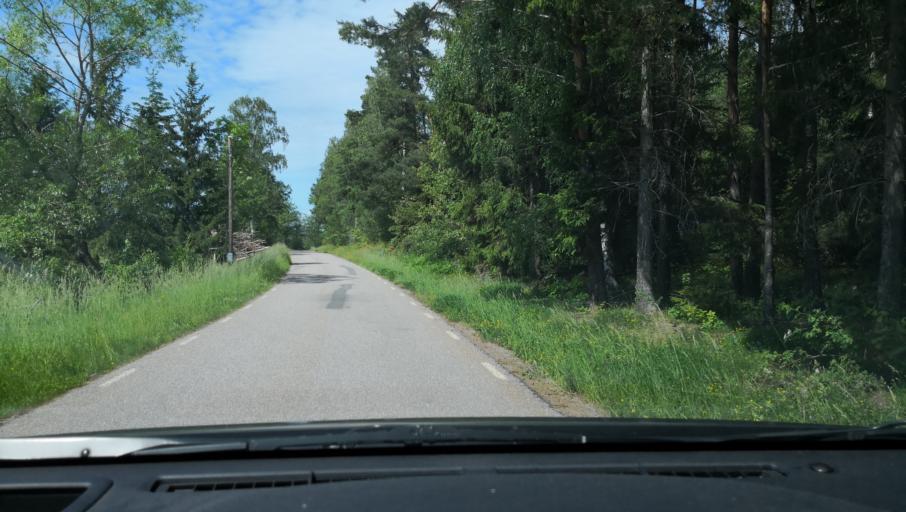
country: SE
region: Stockholm
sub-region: Sigtuna Kommun
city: Sigtuna
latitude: 59.6958
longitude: 17.6434
